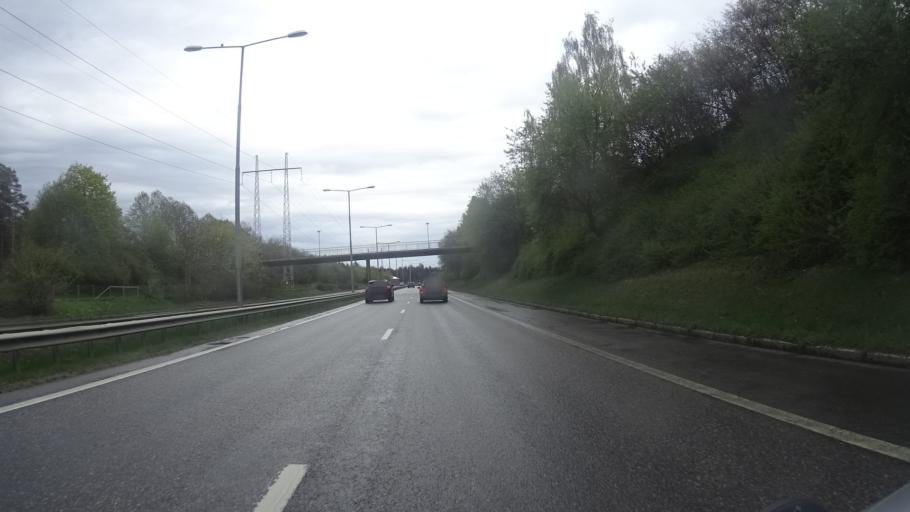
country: SE
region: Stockholm
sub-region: Stockholms Kommun
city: Arsta
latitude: 59.2677
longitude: 18.0583
